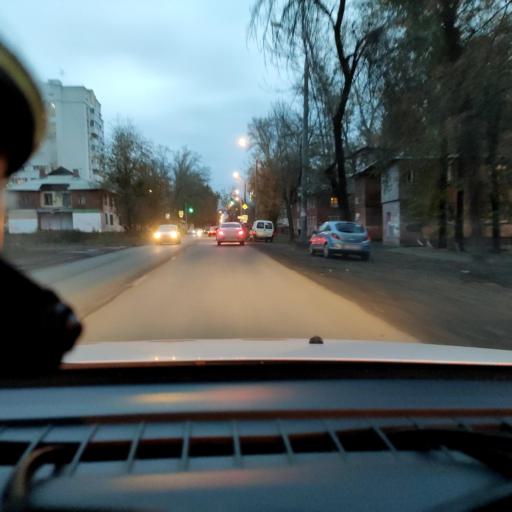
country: RU
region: Samara
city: Samara
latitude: 53.2354
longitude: 50.2619
